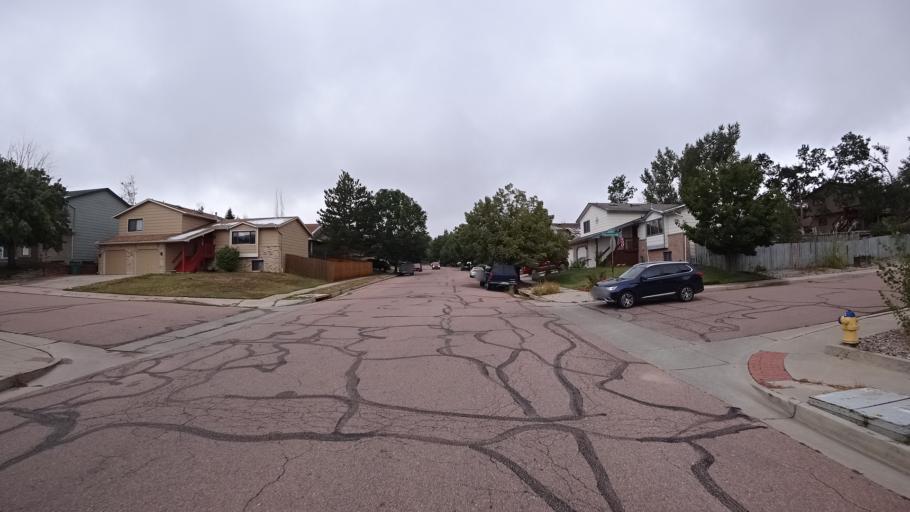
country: US
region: Colorado
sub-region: El Paso County
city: Cimarron Hills
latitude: 38.9235
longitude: -104.7613
